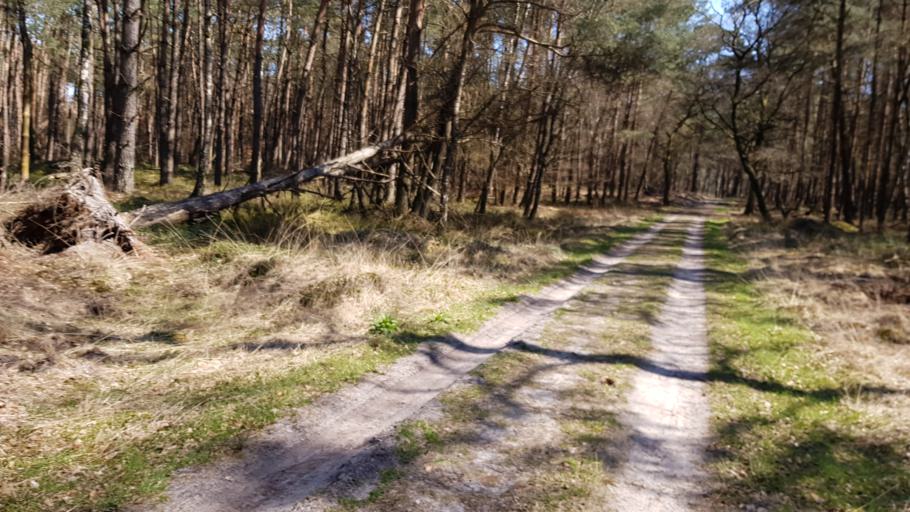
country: NL
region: Gelderland
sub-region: Gemeente Rozendaal
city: Rozendaal
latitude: 52.0613
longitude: 5.9881
